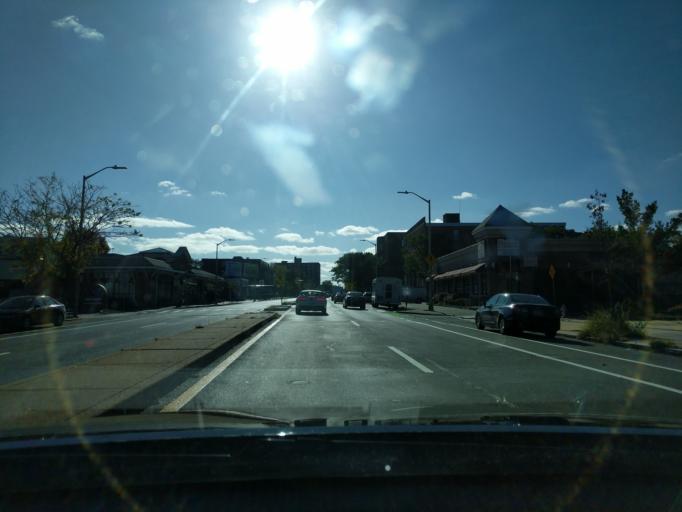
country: US
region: Massachusetts
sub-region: Middlesex County
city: Arlington
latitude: 42.3992
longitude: -71.1324
